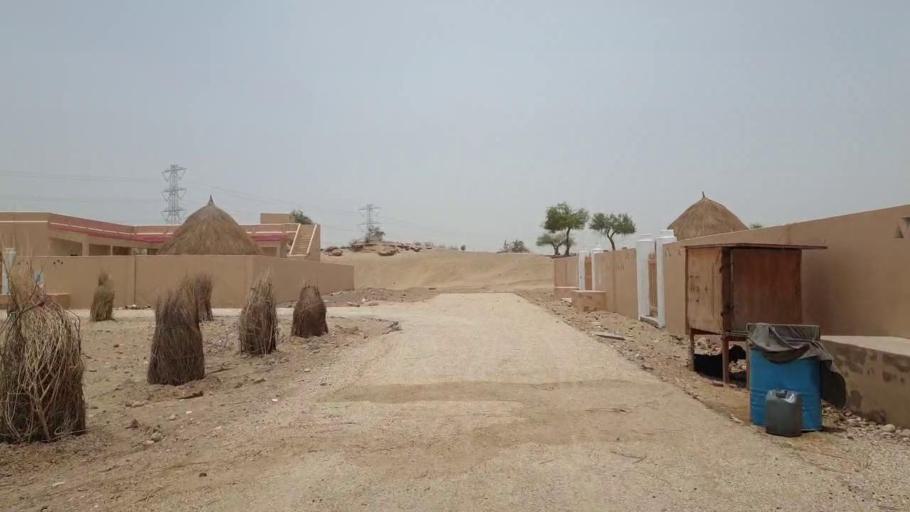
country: PK
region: Sindh
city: Islamkot
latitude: 24.7234
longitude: 70.3331
